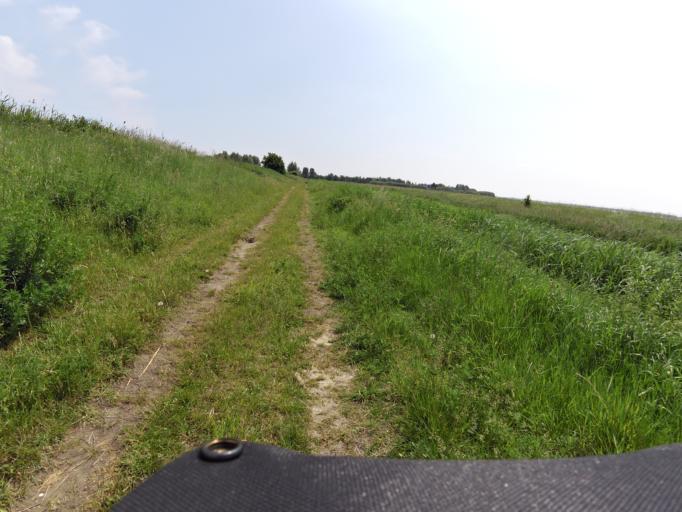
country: NL
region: North Brabant
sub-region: Gemeente Bergen op Zoom
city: Bergen op Zoom
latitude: 51.4836
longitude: 4.2568
